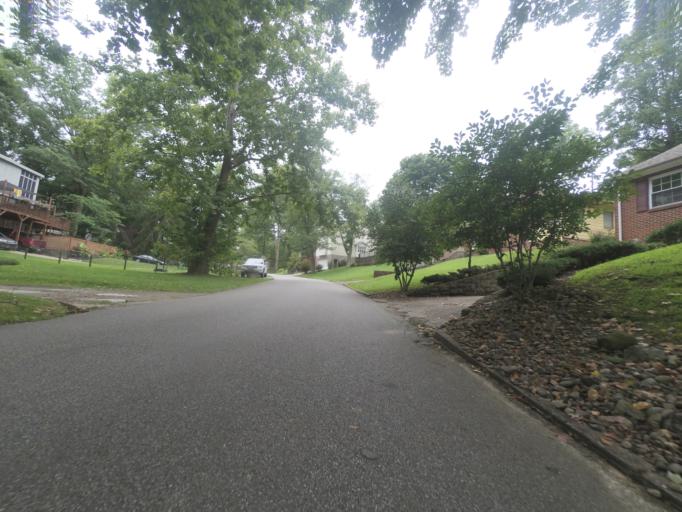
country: US
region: West Virginia
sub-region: Cabell County
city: Huntington
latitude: 38.4002
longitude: -82.4090
